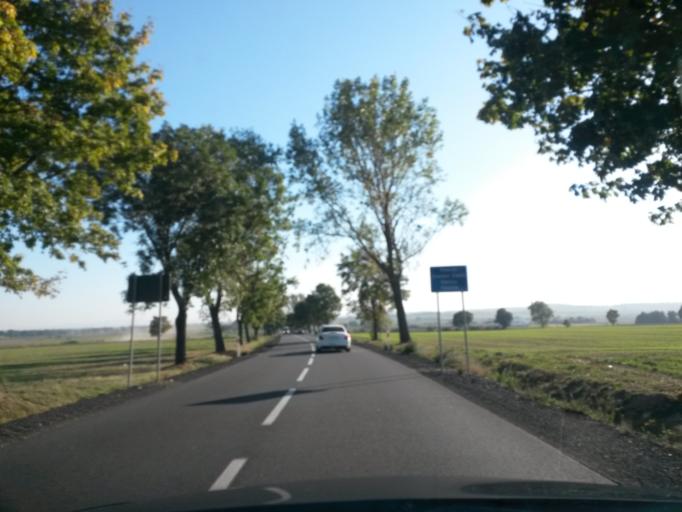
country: PL
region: Lower Silesian Voivodeship
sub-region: Powiat sredzki
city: Udanin
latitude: 51.0709
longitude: 16.4084
